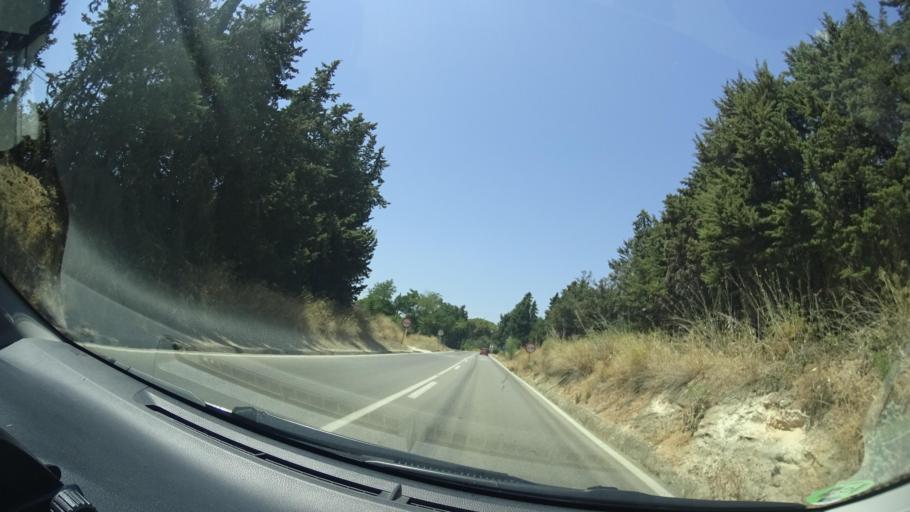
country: ES
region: Andalusia
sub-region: Provincia de Cadiz
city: Jerez de la Frontera
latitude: 36.6607
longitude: -6.1051
